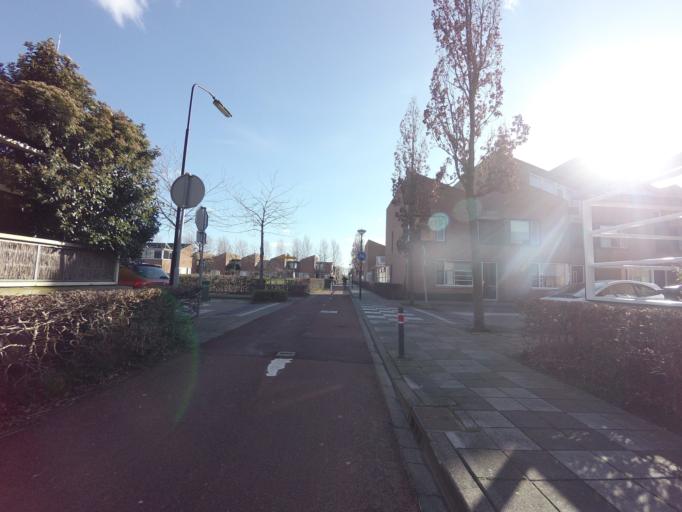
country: NL
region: Utrecht
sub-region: Gemeente IJsselstein
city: IJsselstein
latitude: 52.0122
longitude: 5.0455
